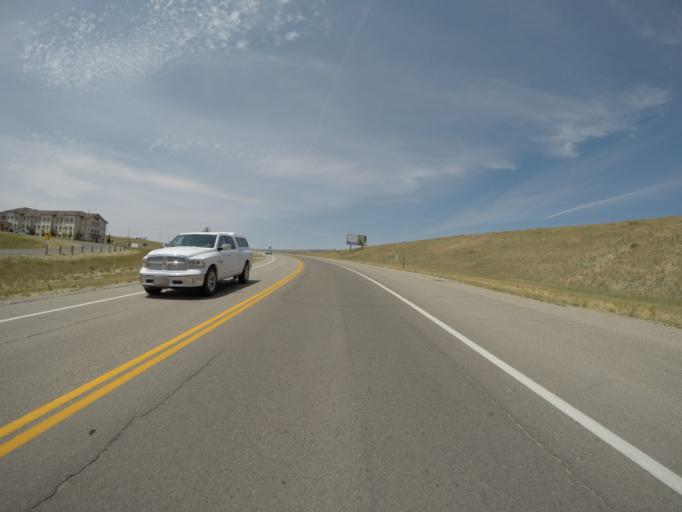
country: US
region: Wyoming
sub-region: Lincoln County
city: Kemmerer
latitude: 41.7737
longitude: -110.5489
